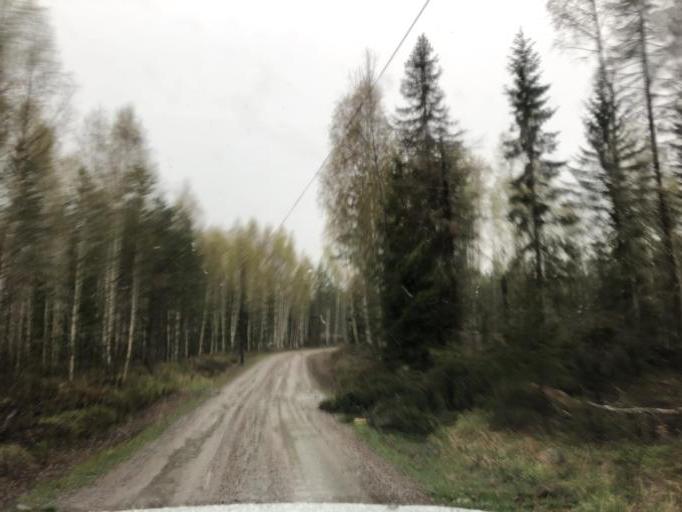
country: SE
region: Uppsala
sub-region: Heby Kommun
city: Tarnsjo
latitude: 60.2032
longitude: 16.8911
